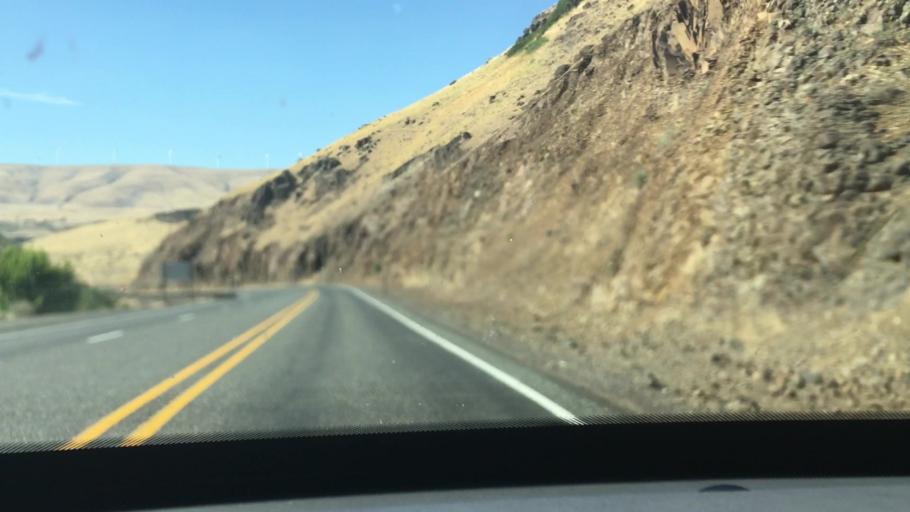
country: US
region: Washington
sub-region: Klickitat County
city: Goldendale
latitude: 45.6615
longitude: -120.8203
